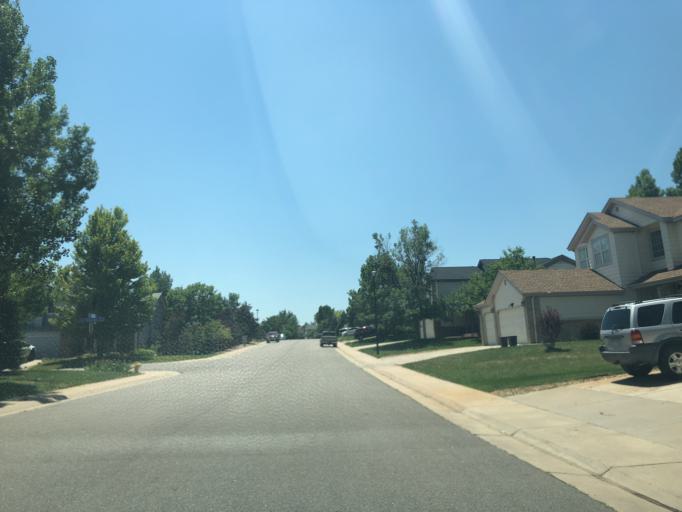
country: US
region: Colorado
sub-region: Arapahoe County
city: Dove Valley
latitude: 39.6233
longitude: -104.7558
